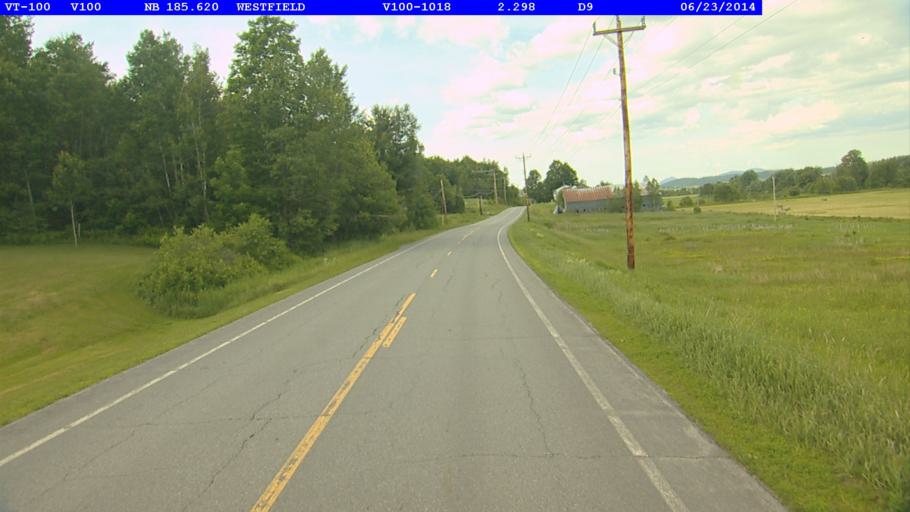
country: US
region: Vermont
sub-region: Orleans County
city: Newport
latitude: 44.8679
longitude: -72.4334
